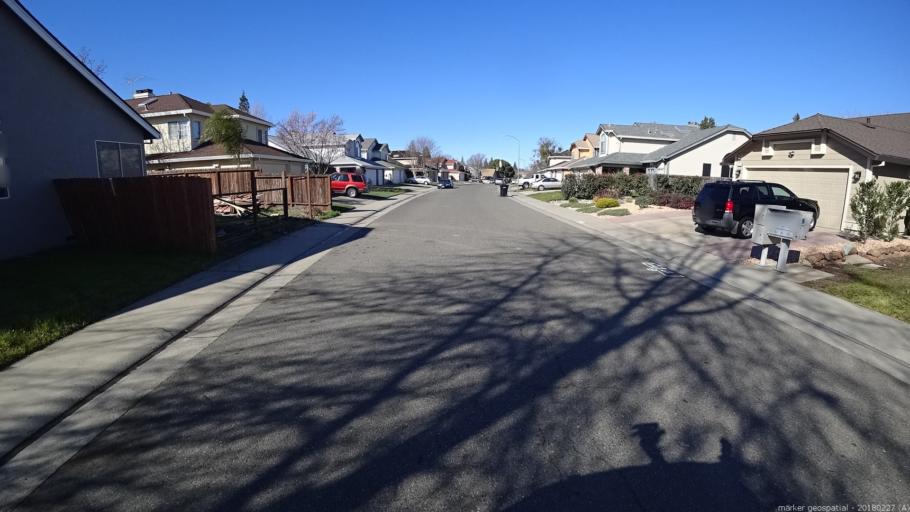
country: US
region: California
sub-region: Sacramento County
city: North Highlands
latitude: 38.7234
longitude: -121.3702
